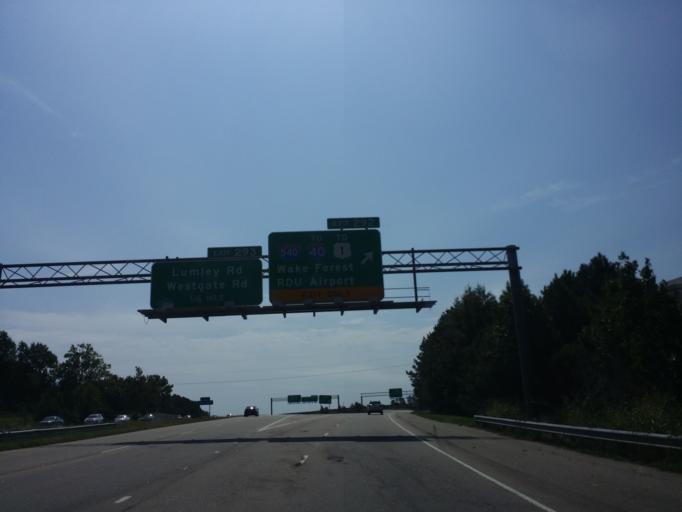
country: US
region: North Carolina
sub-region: Wake County
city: Morrisville
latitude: 35.9091
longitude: -78.7772
